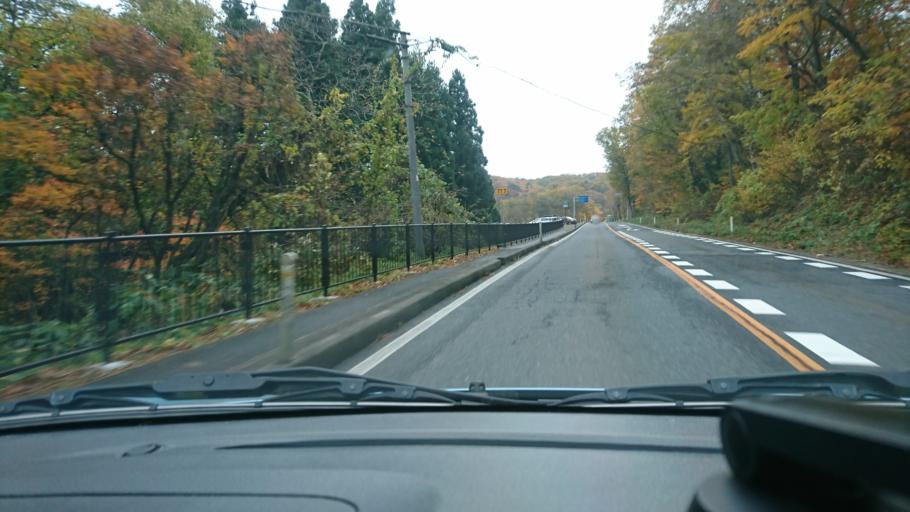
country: JP
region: Miyagi
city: Furukawa
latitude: 38.7338
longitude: 140.6876
